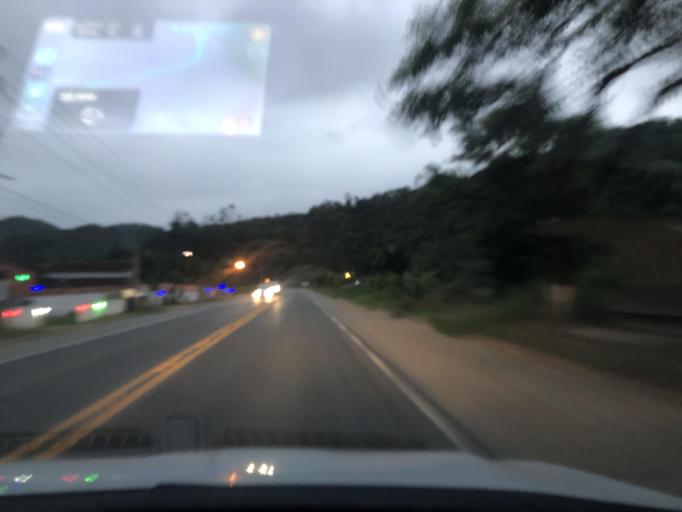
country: BR
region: Santa Catarina
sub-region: Jaragua Do Sul
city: Jaragua do Sul
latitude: -26.6487
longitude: -49.0201
